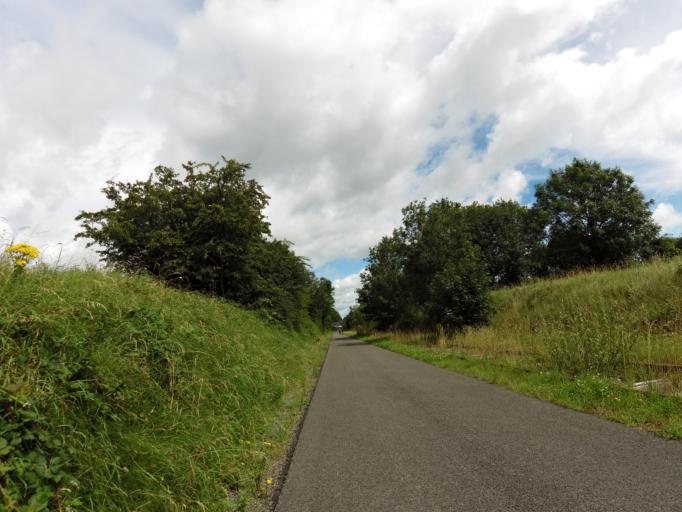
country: IE
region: Leinster
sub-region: An Iarmhi
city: Kilbeggan
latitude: 53.4655
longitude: -7.5019
